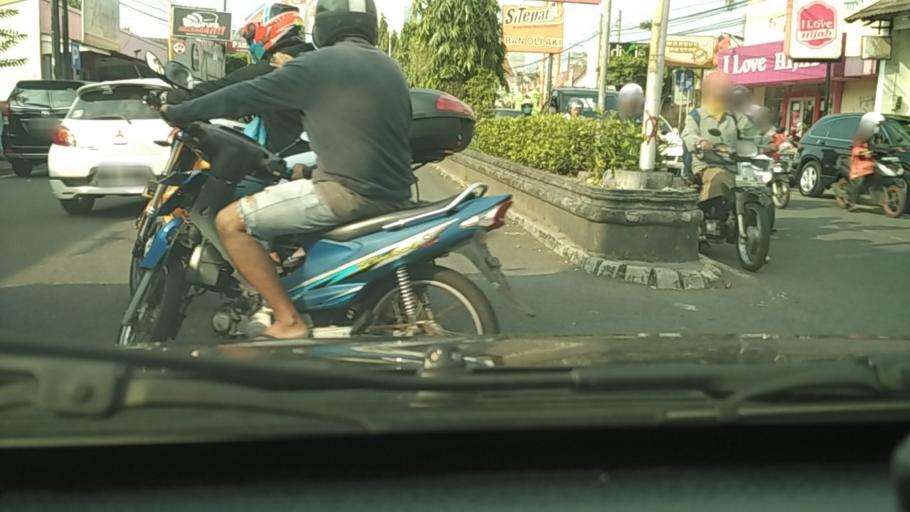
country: ID
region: Daerah Istimewa Yogyakarta
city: Yogyakarta
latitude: -7.7702
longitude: 110.3903
